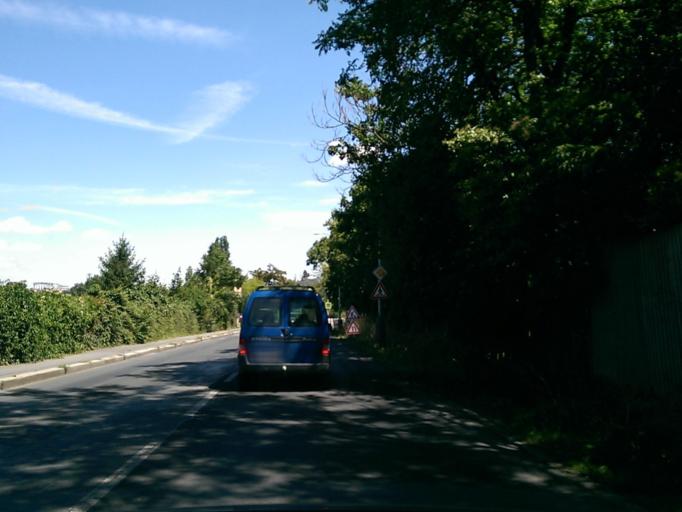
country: CZ
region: Praha
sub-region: Praha 8
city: Liben
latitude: 50.0990
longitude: 14.4829
